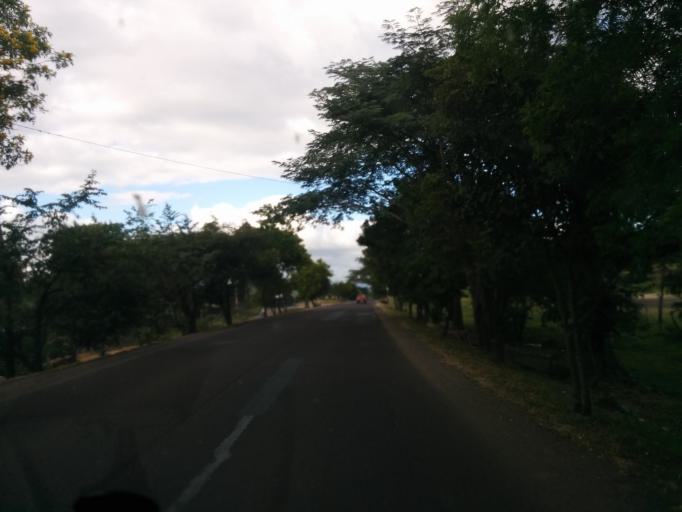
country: NI
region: Esteli
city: Esteli
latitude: 13.1571
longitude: -86.3700
